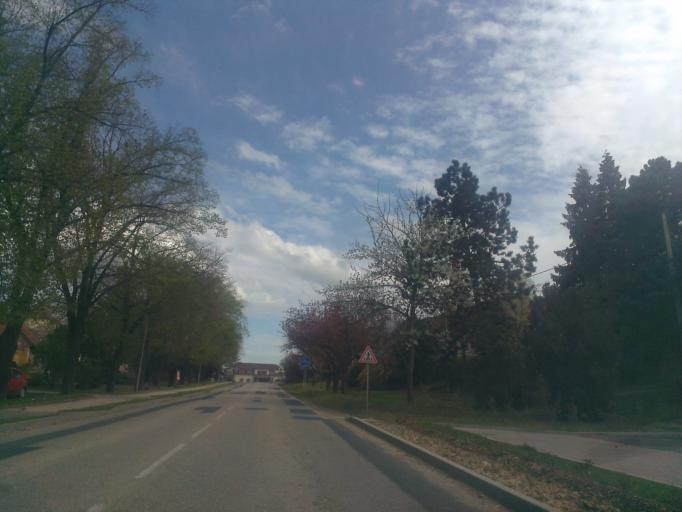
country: CZ
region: South Moravian
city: Orechov
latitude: 49.1110
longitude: 16.5238
